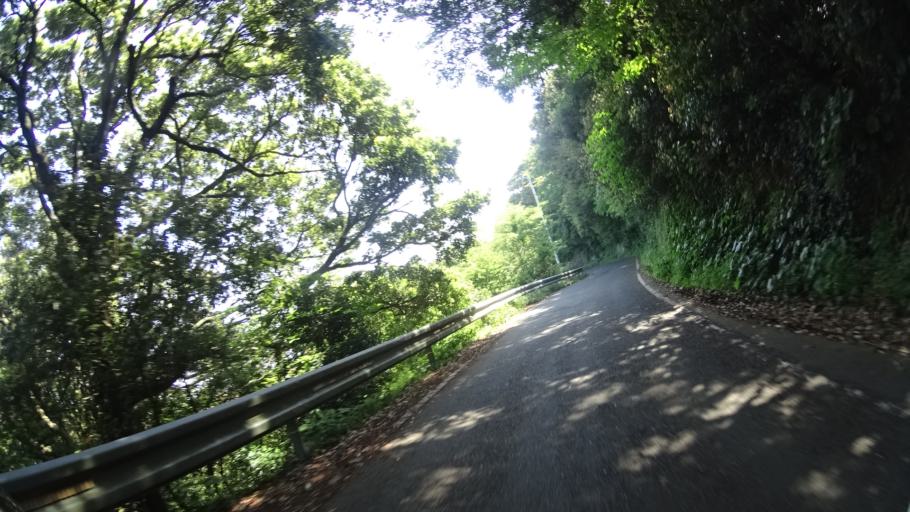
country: JP
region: Ehime
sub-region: Nishiuwa-gun
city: Ikata-cho
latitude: 33.3765
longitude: 132.0610
